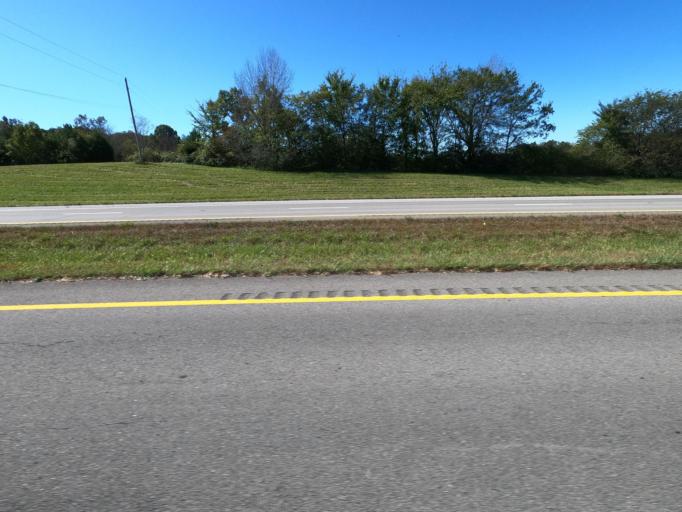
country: US
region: Tennessee
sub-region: Lawrence County
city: Lawrenceburg
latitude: 35.3881
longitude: -87.2758
